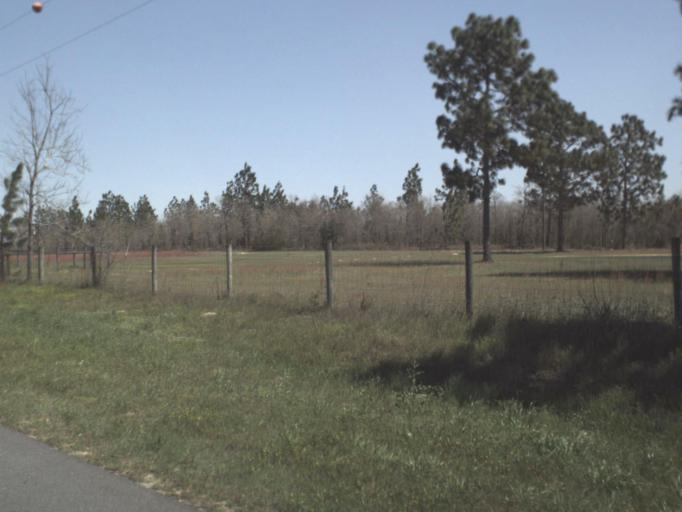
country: US
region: Florida
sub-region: Bay County
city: Youngstown
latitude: 30.4272
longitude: -85.2931
